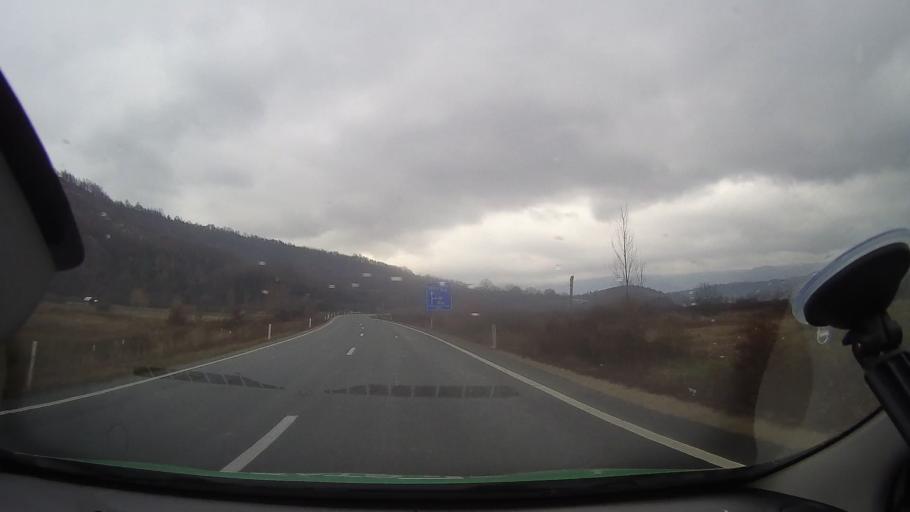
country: RO
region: Hunedoara
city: Vata de Jos
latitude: 46.2142
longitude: 22.5776
